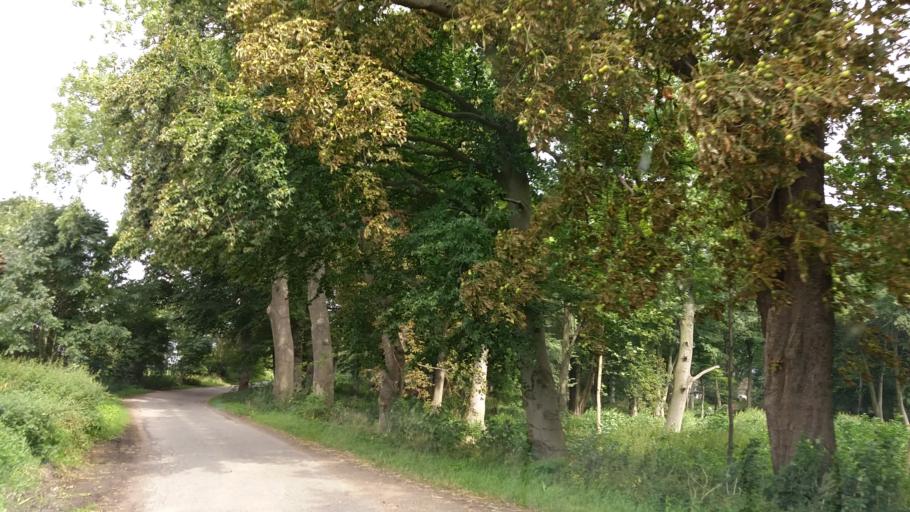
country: PL
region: West Pomeranian Voivodeship
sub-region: Powiat choszczenski
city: Krzecin
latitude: 53.1105
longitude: 15.4942
